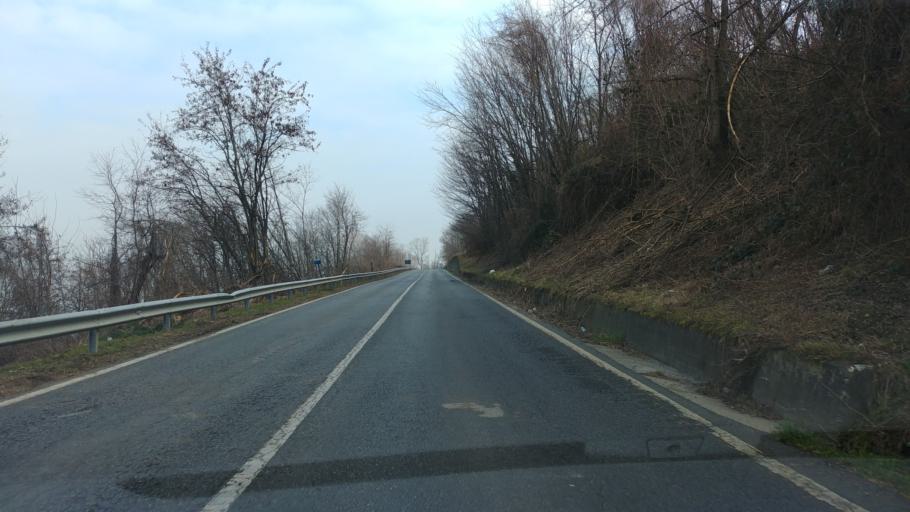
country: IT
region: Piedmont
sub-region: Provincia di Cuneo
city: Castelletto Stura
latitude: 44.4480
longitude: 7.6415
